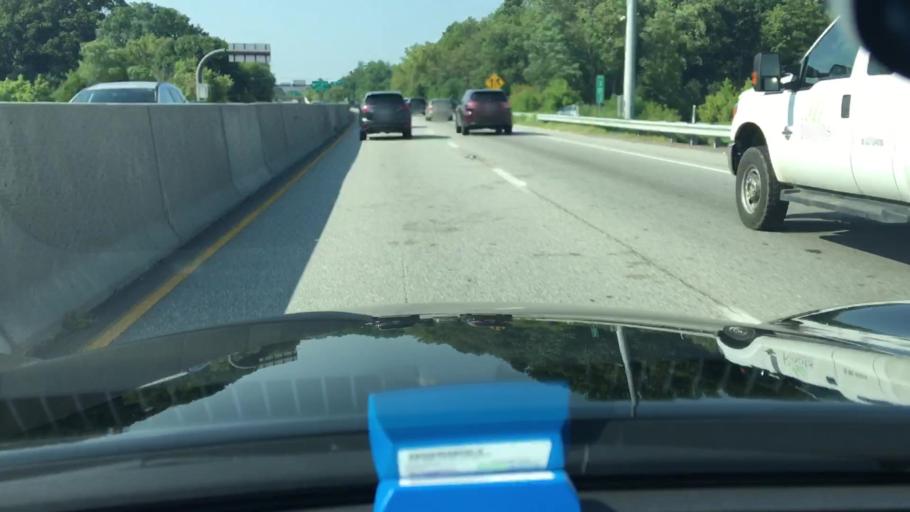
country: US
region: Pennsylvania
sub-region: Chester County
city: West Chester
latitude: 39.9725
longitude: -75.5835
